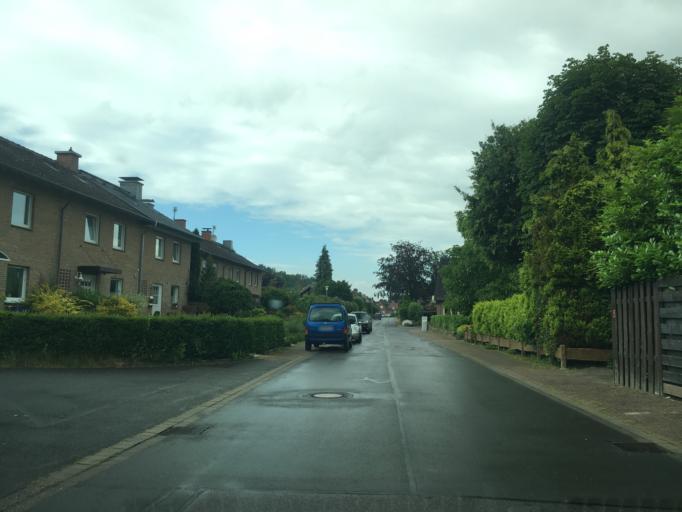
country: DE
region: North Rhine-Westphalia
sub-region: Regierungsbezirk Munster
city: Greven
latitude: 52.0339
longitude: 7.6149
